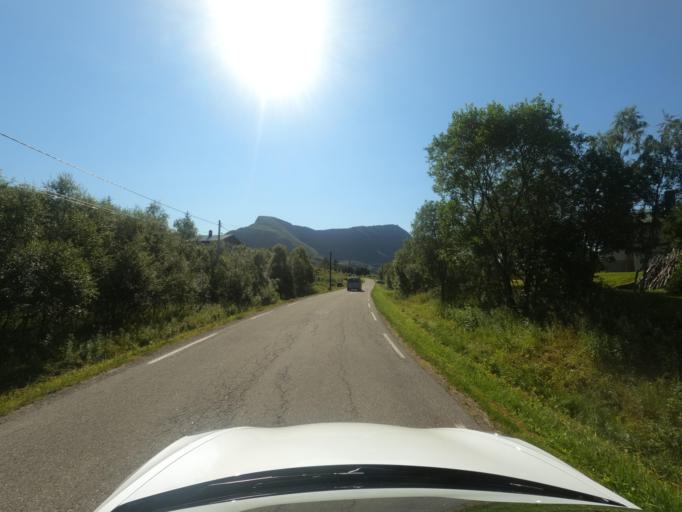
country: NO
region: Nordland
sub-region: Hadsel
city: Stokmarknes
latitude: 68.3075
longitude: 14.9967
